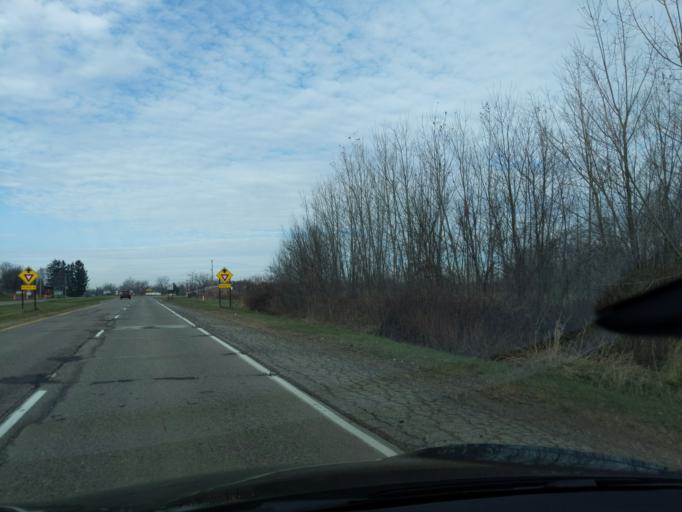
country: US
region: Michigan
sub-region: Ingham County
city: Holt
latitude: 42.6303
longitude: -84.5054
